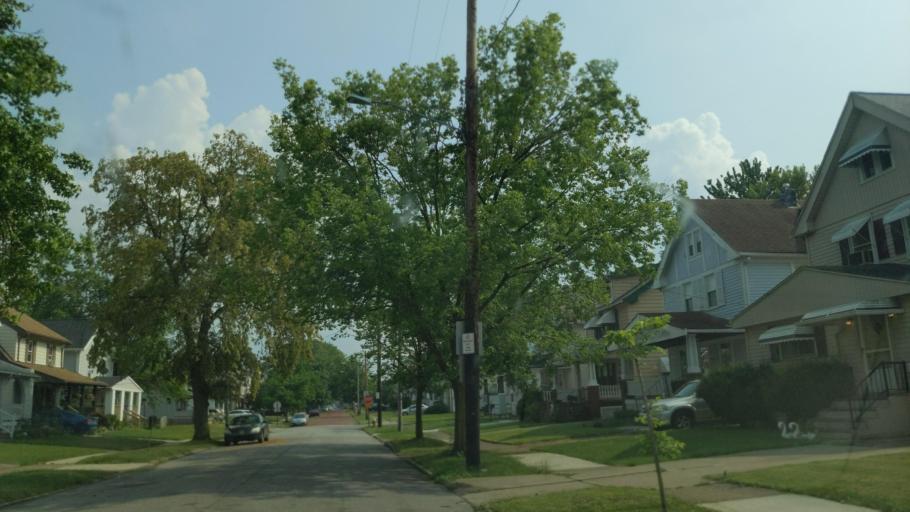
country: US
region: Ohio
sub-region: Cuyahoga County
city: Lakewood
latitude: 41.4571
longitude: -81.7767
